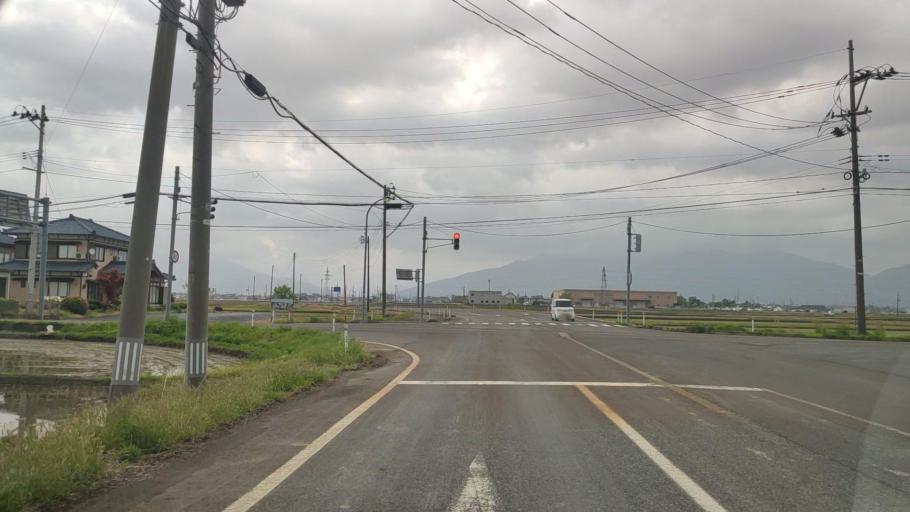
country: JP
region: Niigata
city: Gosen
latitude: 37.7290
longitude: 139.1613
